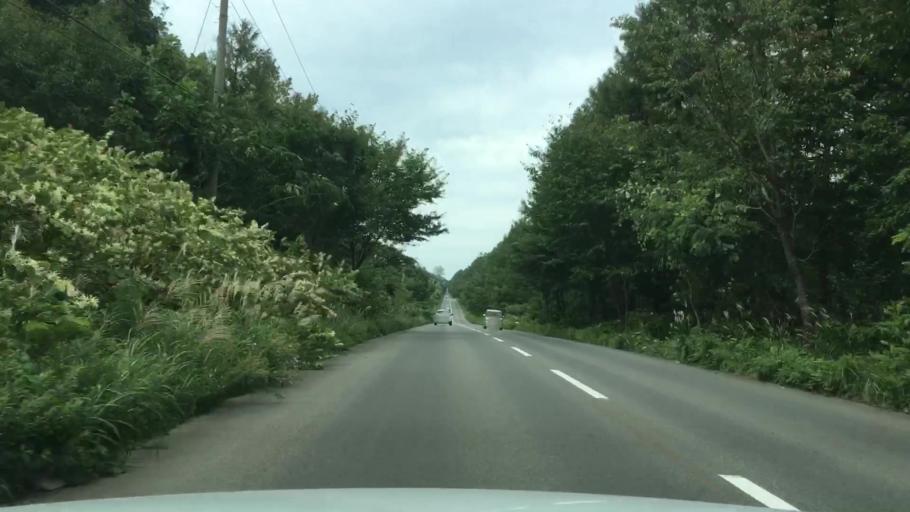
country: JP
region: Aomori
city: Shimokizukuri
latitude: 40.7124
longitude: 140.3268
